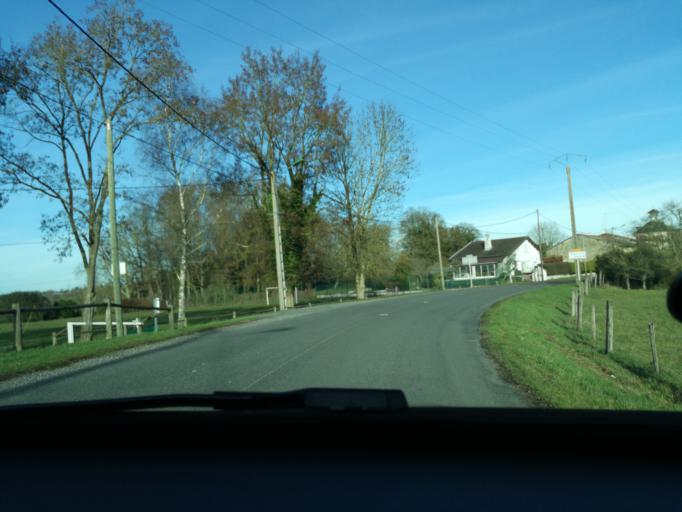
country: FR
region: Lorraine
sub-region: Departement de la Meuse
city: Revigny-sur-Ornain
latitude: 48.8214
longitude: 5.0425
